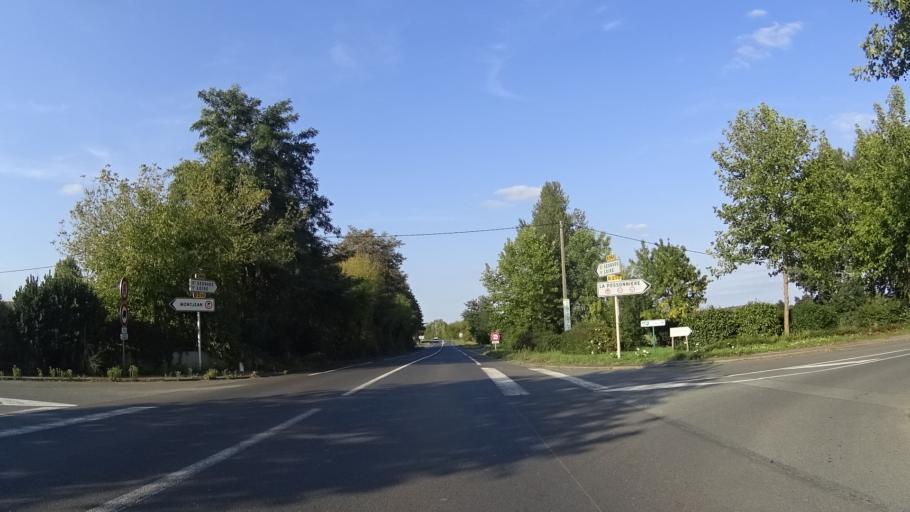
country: FR
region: Pays de la Loire
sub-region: Departement de Maine-et-Loire
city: Chalonnes-sur-Loire
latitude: 47.3703
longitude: -0.7530
